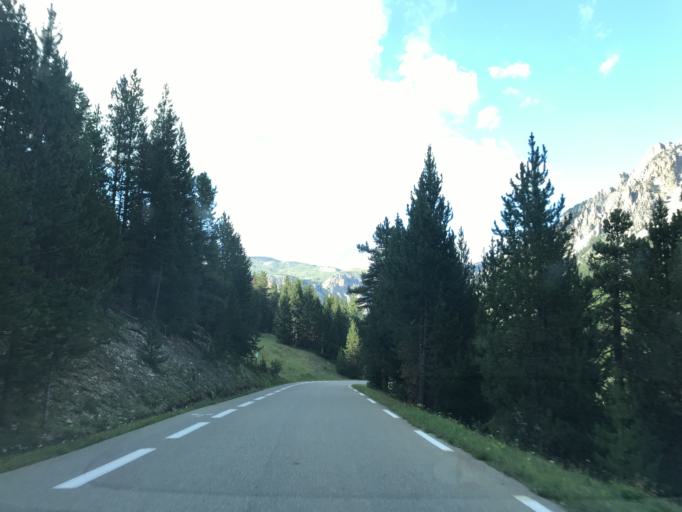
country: IT
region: Piedmont
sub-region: Provincia di Torino
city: Claviere
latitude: 44.8488
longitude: 6.7247
